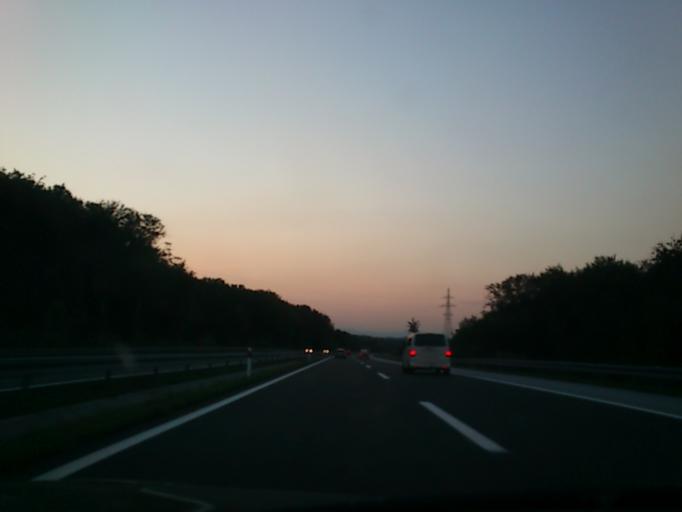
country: HR
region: Karlovacka
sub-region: Grad Ogulin
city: Ogulin
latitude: 45.3615
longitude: 15.2745
